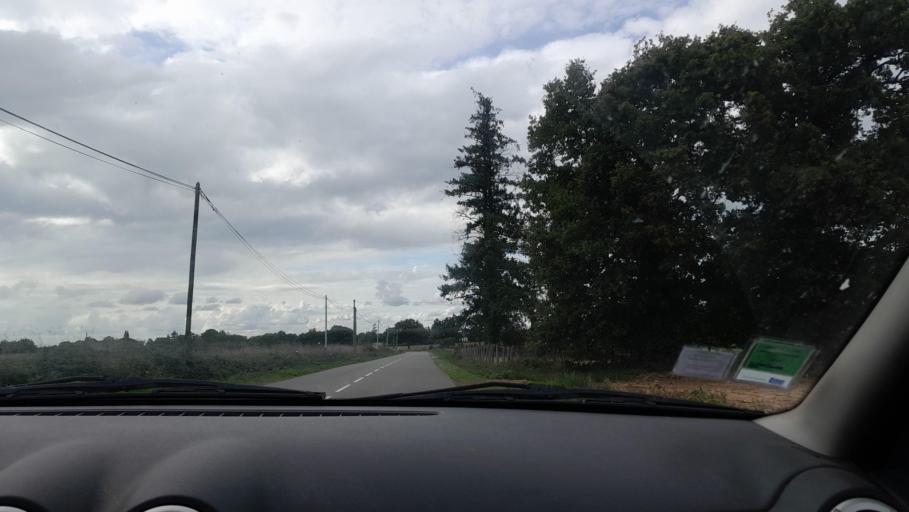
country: FR
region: Brittany
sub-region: Departement d'Ille-et-Vilaine
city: Argentre-du-Plessis
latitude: 48.0530
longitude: -1.1187
